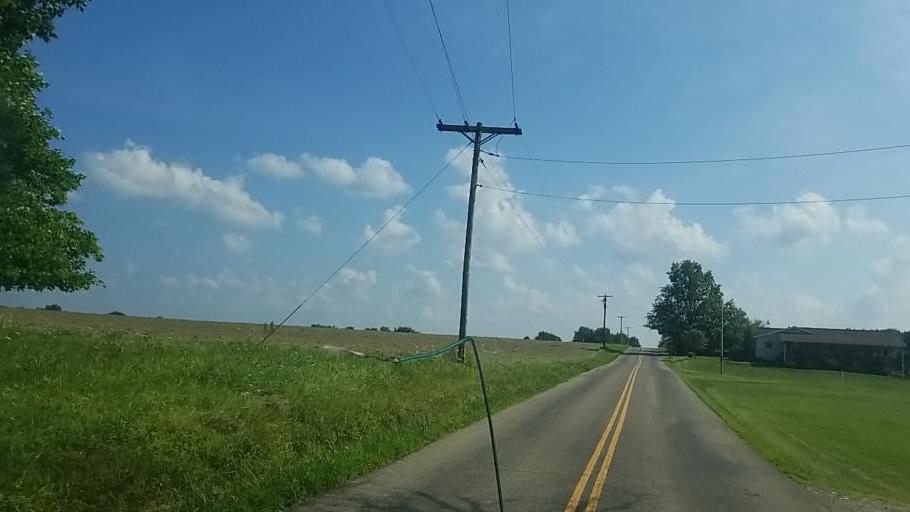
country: US
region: Ohio
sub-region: Knox County
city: Oak Hill
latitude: 40.3156
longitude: -82.2783
